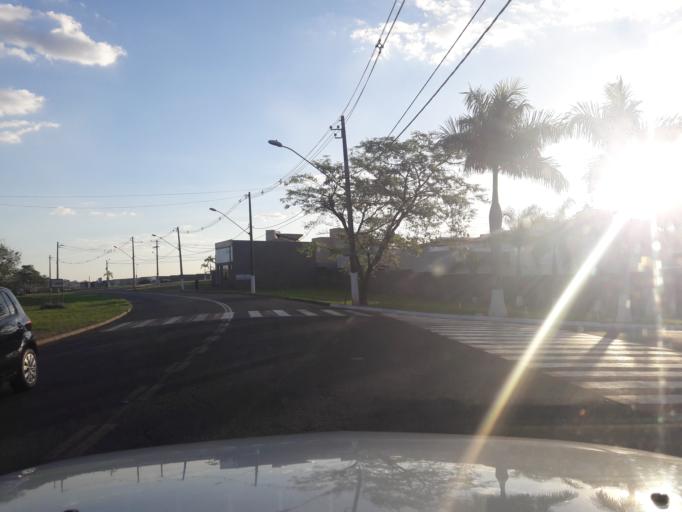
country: BR
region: Sao Paulo
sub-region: Moji-Guacu
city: Mogi-Gaucu
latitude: -22.3933
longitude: -46.9498
